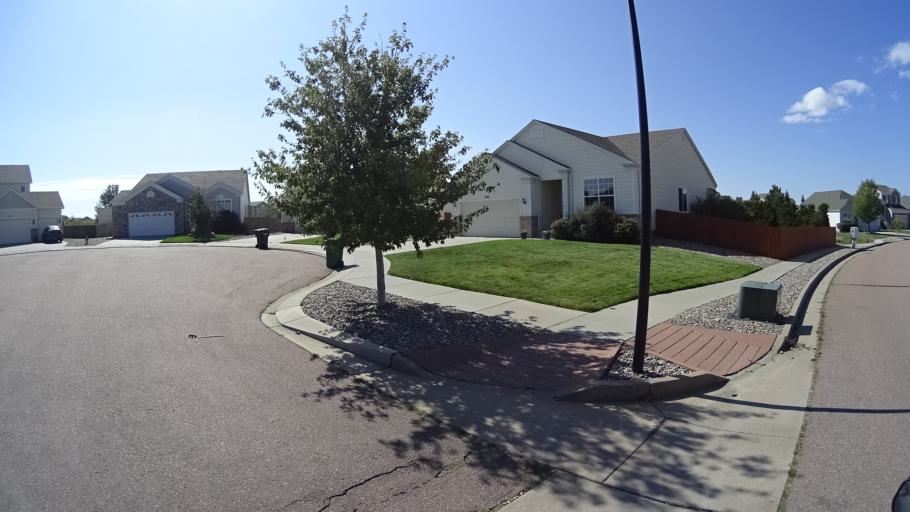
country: US
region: Colorado
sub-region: El Paso County
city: Cimarron Hills
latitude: 38.9271
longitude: -104.6958
